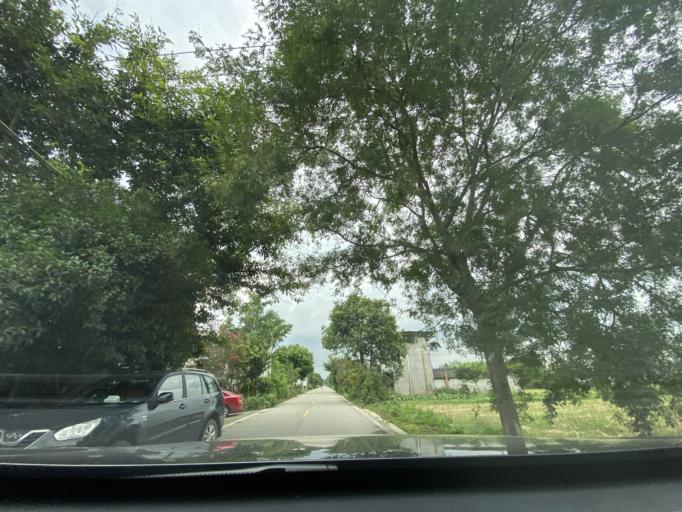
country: CN
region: Sichuan
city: Wujin
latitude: 30.3778
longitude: 103.9681
